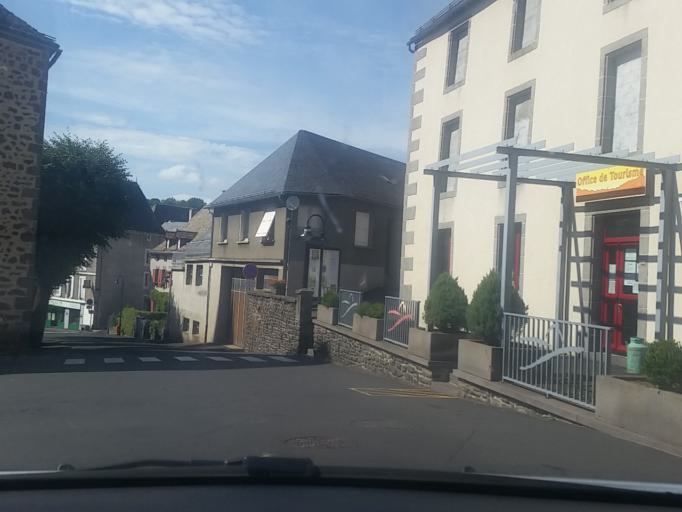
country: FR
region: Auvergne
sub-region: Departement du Cantal
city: Pierrefort
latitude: 44.9208
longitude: 2.8402
